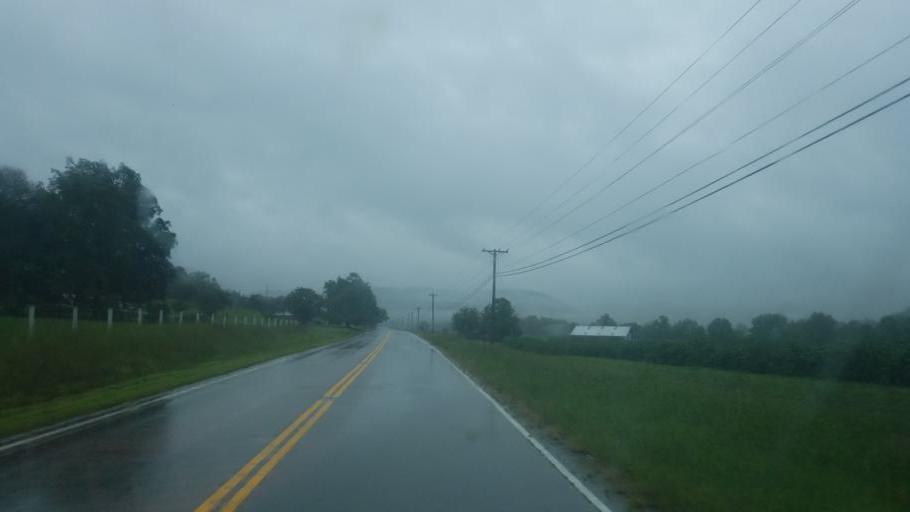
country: US
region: Kentucky
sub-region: Fleming County
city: Flemingsburg
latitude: 38.3225
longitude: -83.5819
